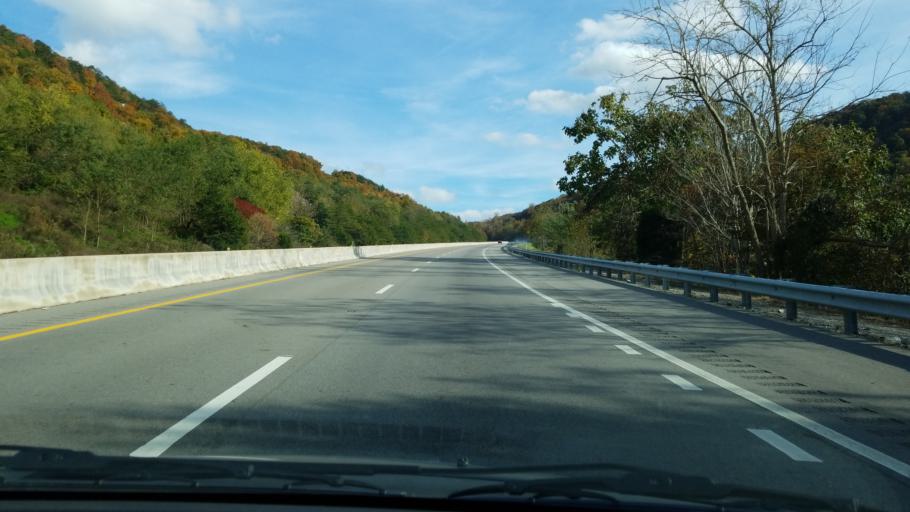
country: US
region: Tennessee
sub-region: Sequatchie County
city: Dunlap
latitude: 35.3614
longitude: -85.3231
